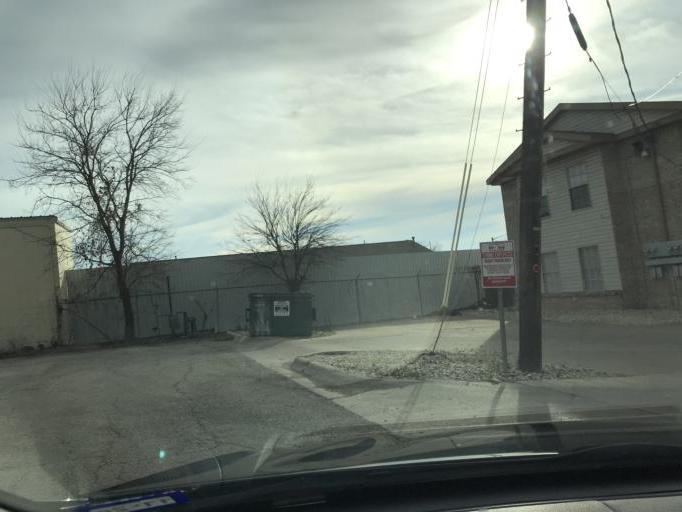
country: US
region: Texas
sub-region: Denton County
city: Denton
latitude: 33.2129
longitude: -97.1568
